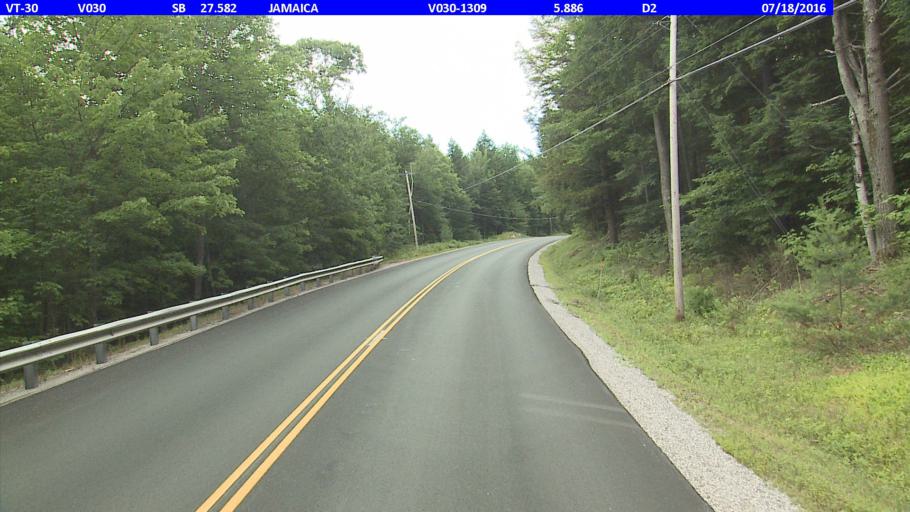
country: US
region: Vermont
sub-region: Windham County
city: Dover
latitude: 43.1172
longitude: -72.8044
